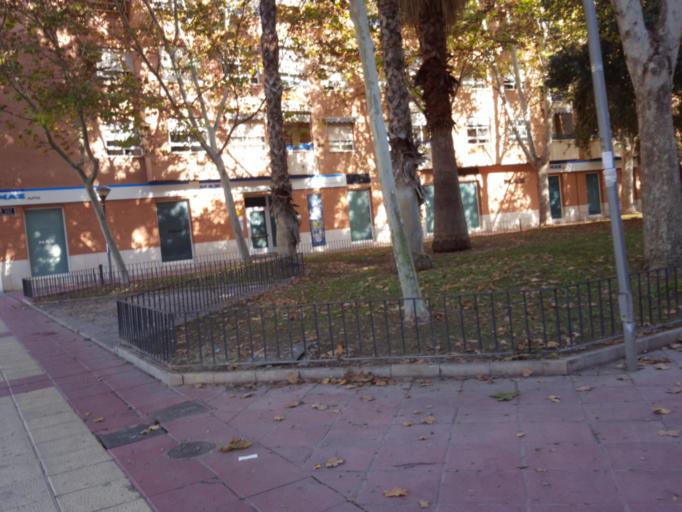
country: ES
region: Murcia
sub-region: Murcia
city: Murcia
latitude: 37.9980
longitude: -1.1257
